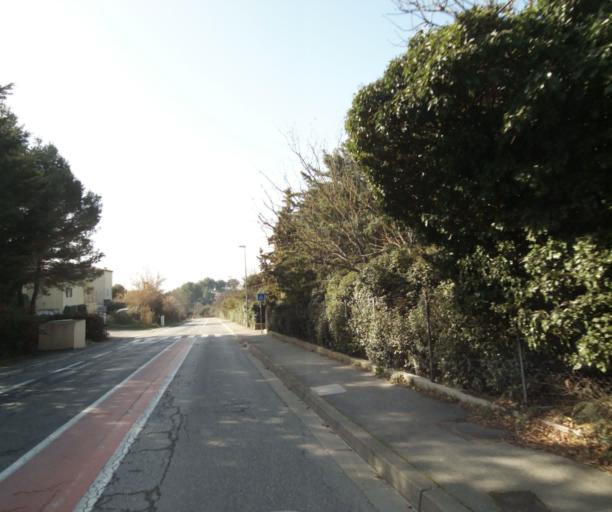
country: FR
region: Provence-Alpes-Cote d'Azur
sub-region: Departement des Bouches-du-Rhone
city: Aix-en-Provence
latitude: 43.5482
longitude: 5.4555
